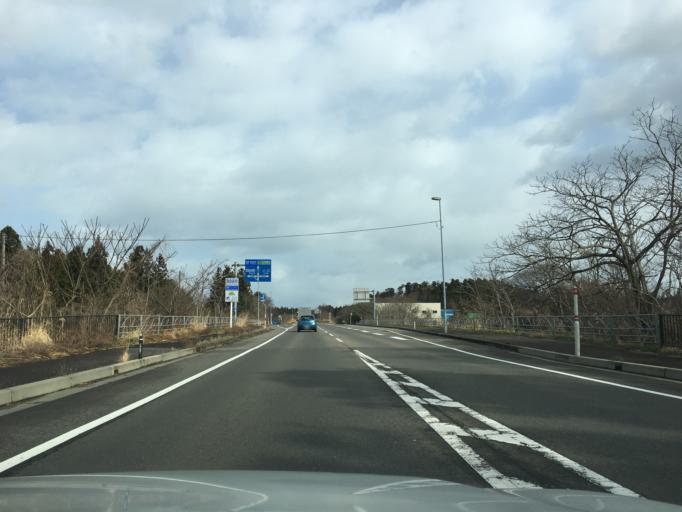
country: JP
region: Yamagata
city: Yuza
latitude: 39.2539
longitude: 139.9269
